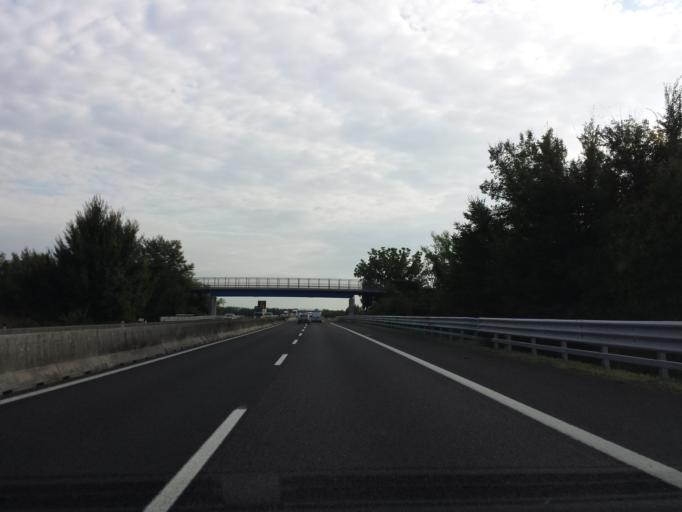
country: IT
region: Veneto
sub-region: Provincia di Padova
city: Pozzonovo
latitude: 45.1984
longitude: 11.7748
